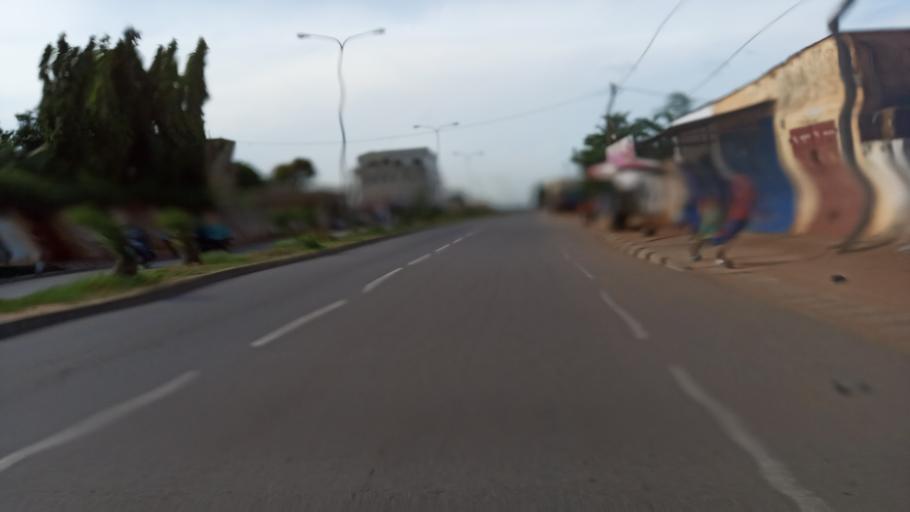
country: TG
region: Maritime
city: Lome
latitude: 6.1743
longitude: 1.2675
